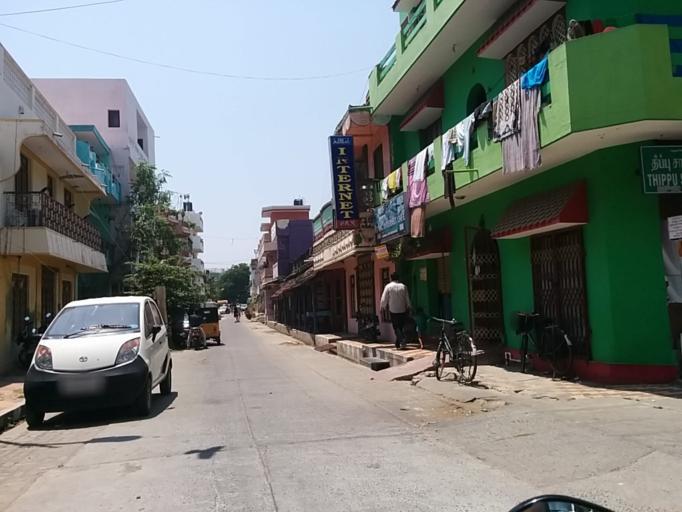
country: IN
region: Pondicherry
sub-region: Puducherry
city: Puducherry
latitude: 11.9269
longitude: 79.8288
